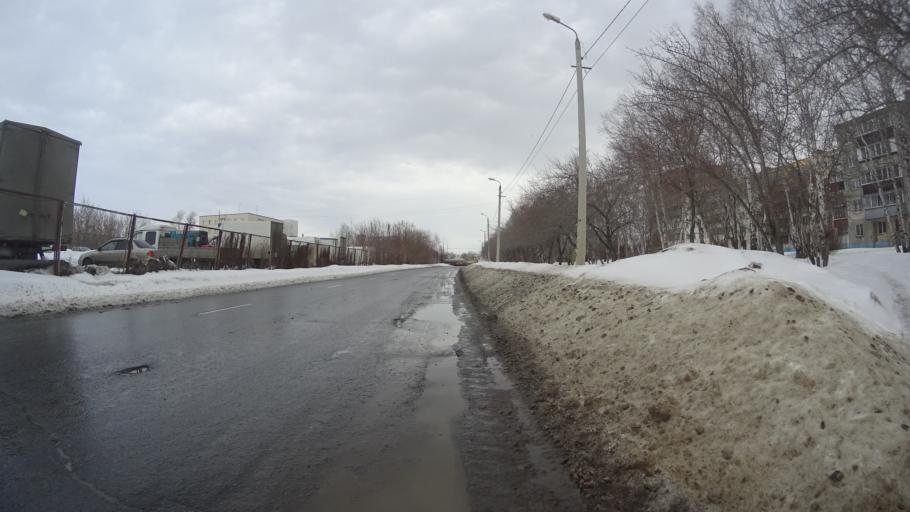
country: RU
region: Chelyabinsk
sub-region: Gorod Chelyabinsk
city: Chelyabinsk
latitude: 55.2011
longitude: 61.3245
